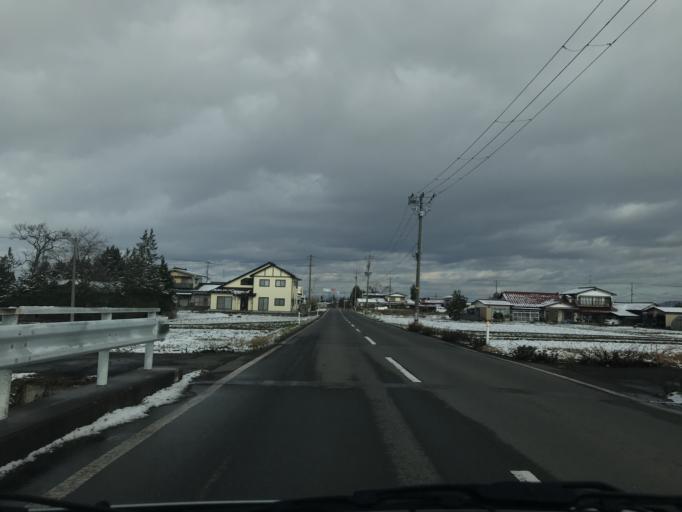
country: JP
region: Iwate
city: Mizusawa
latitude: 39.1611
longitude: 141.1116
